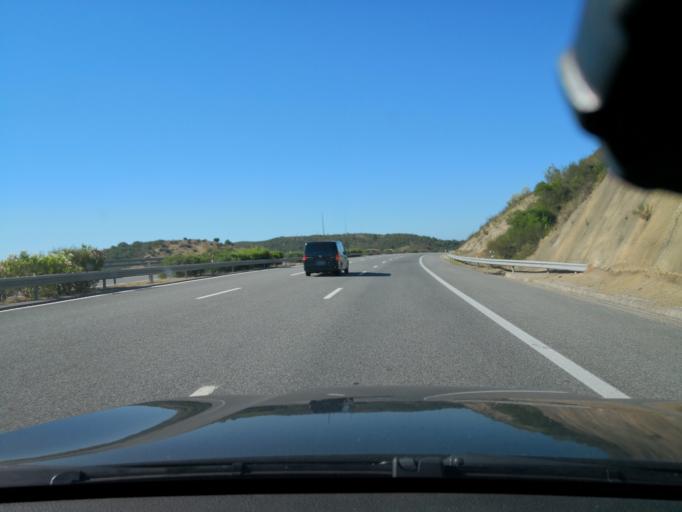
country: PT
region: Faro
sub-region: Silves
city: Sao Bartolomeu de Messines
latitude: 37.3500
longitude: -8.2568
